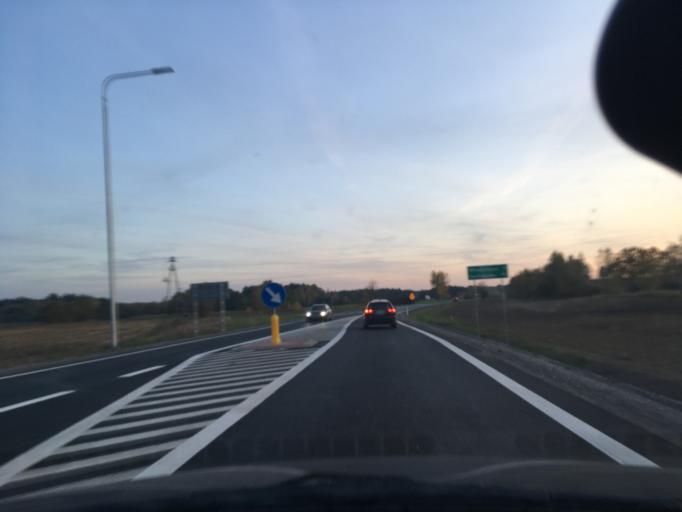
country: PL
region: Masovian Voivodeship
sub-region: Powiat plocki
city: Wyszogrod
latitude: 52.3559
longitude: 20.2090
